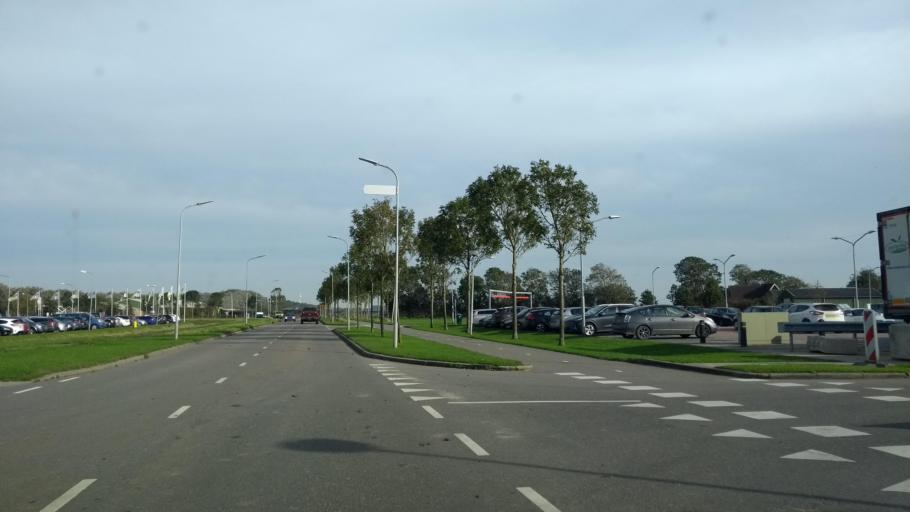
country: NL
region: North Holland
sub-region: Gemeente Schagen
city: Harenkarspel
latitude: 52.7152
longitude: 4.7346
